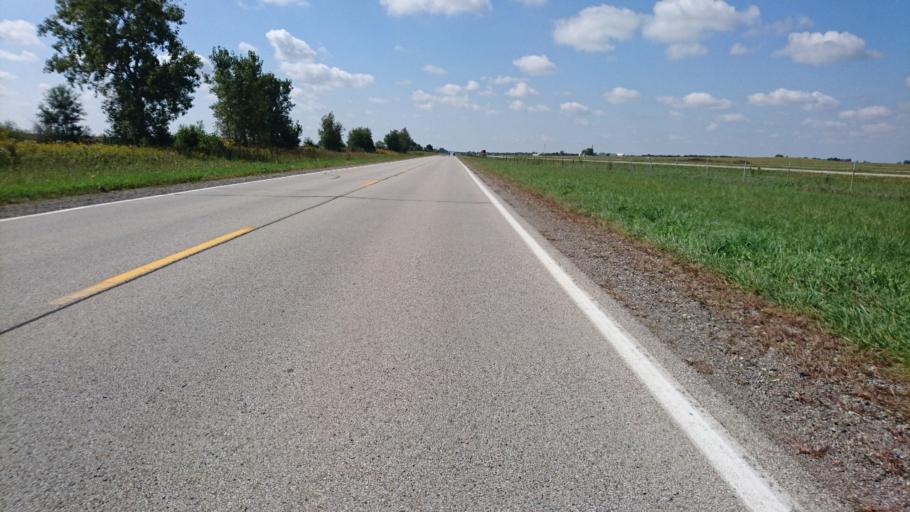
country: US
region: Illinois
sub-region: McLean County
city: Lexington
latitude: 40.6171
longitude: -88.8210
